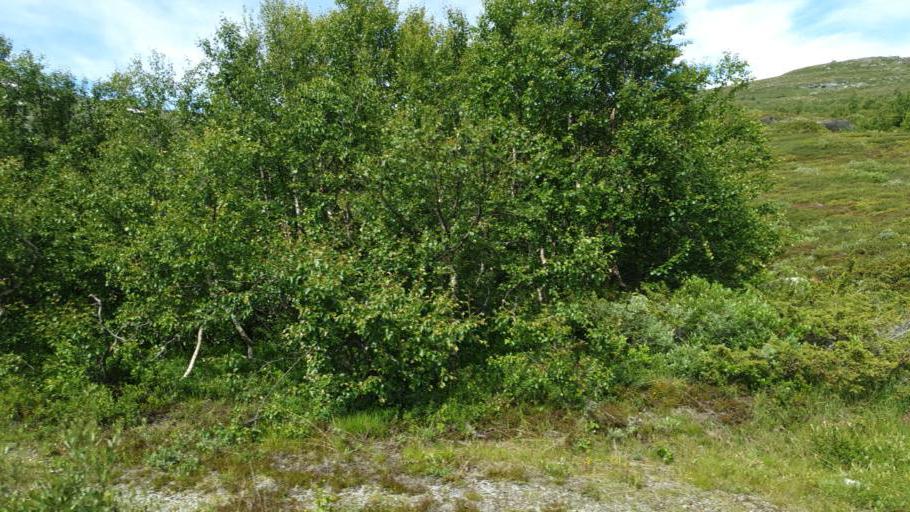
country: NO
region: Oppland
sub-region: Lom
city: Fossbergom
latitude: 61.5120
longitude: 8.8451
